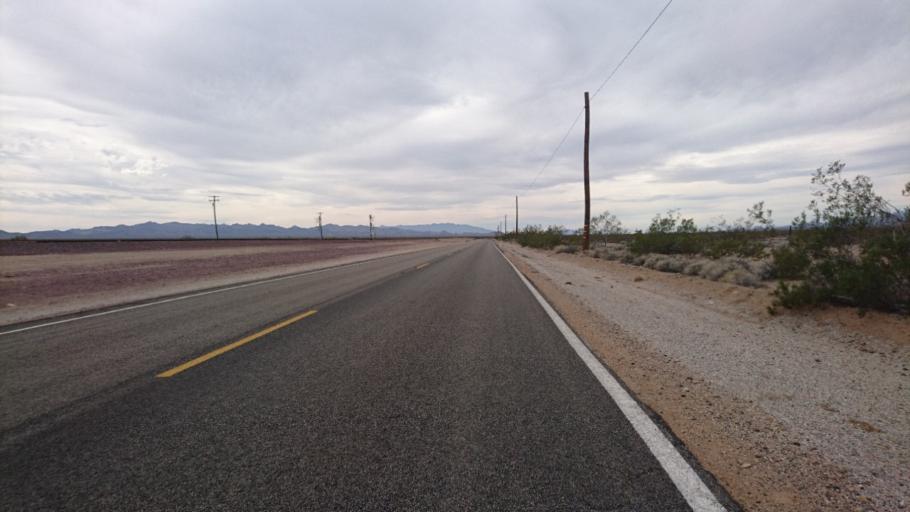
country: US
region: California
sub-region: San Bernardino County
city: Needles
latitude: 34.8934
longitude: -115.0956
